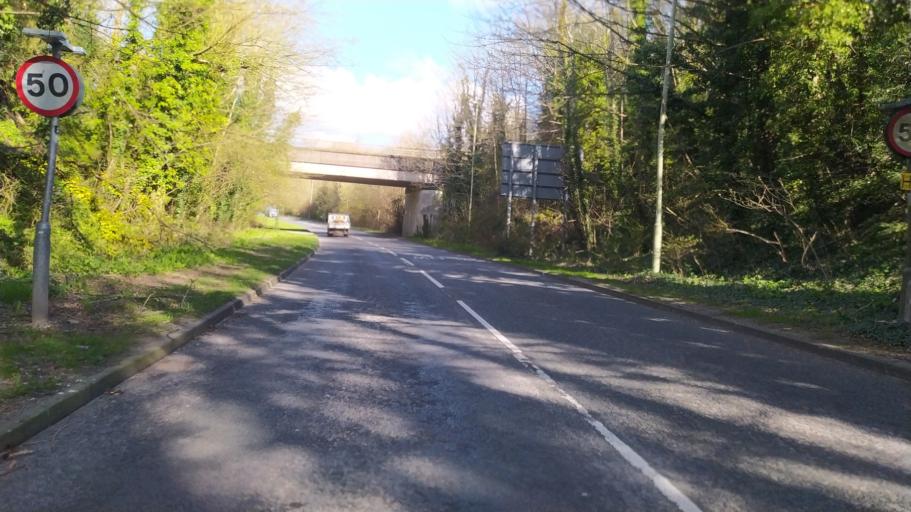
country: GB
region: England
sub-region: Hampshire
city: Andover
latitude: 51.2138
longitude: -1.4860
